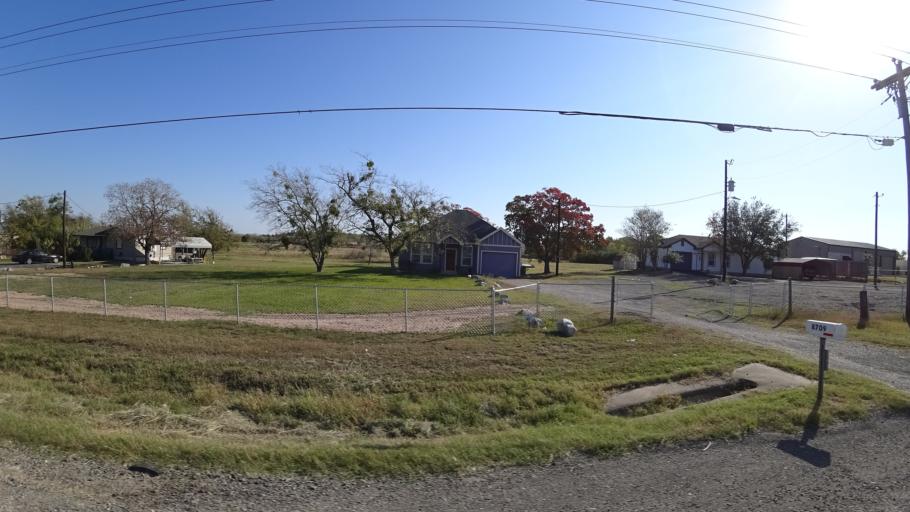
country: US
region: Texas
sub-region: Travis County
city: Onion Creek
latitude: 30.1278
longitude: -97.6957
